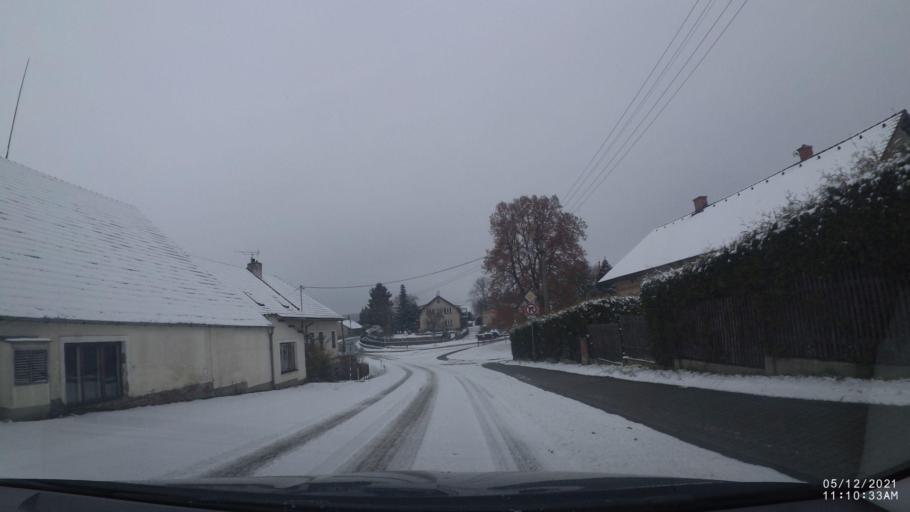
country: CZ
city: Solnice
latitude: 50.1789
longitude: 16.2238
